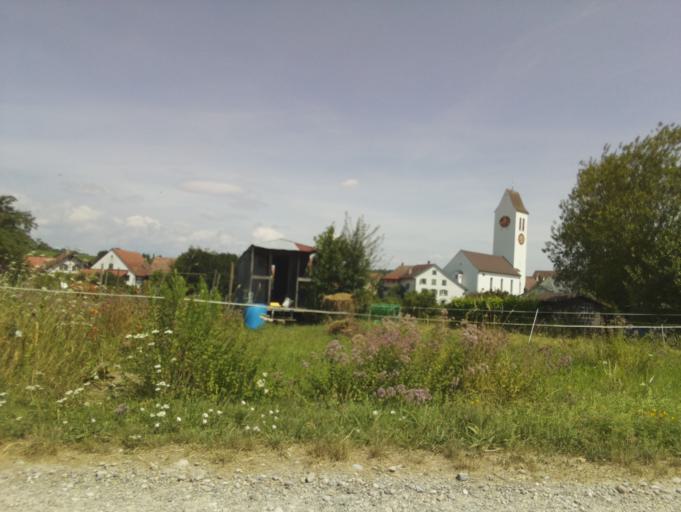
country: CH
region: Zurich
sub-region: Bezirk Andelfingen
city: Kleinandelfingen
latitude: 47.6092
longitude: 8.7243
